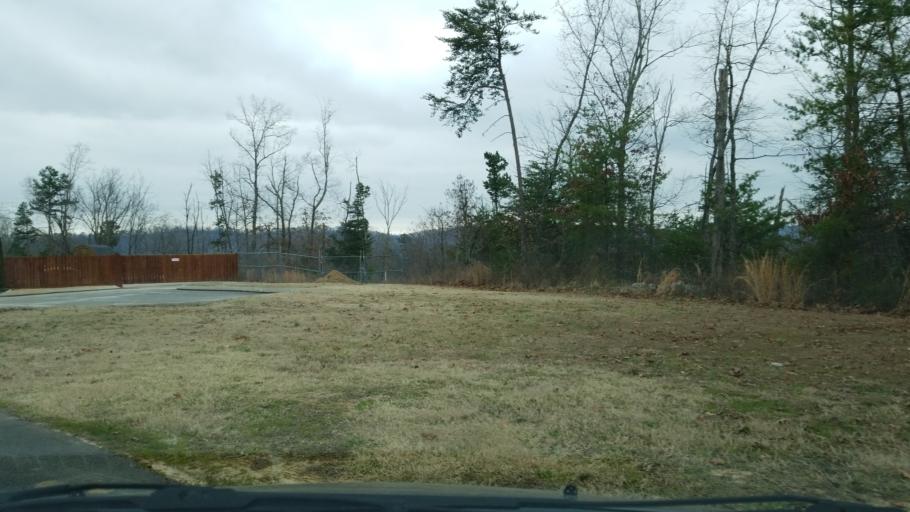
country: US
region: Tennessee
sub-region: Hamilton County
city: Collegedale
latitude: 35.0630
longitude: -85.0844
